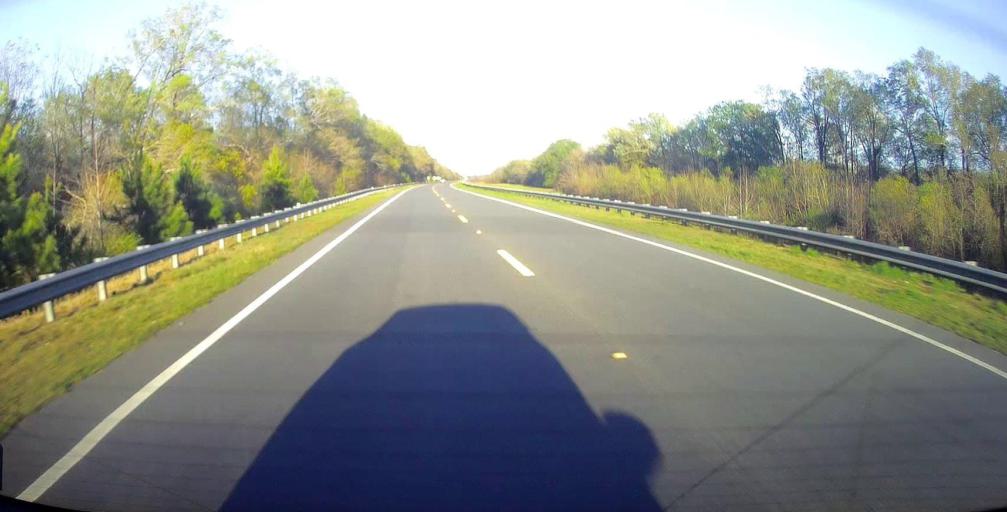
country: US
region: Georgia
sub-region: Wilcox County
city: Abbeville
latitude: 31.9942
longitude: -83.2935
